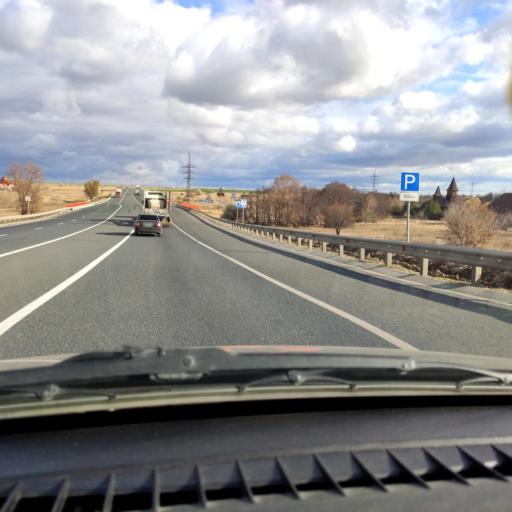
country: RU
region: Samara
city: Varlamovo
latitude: 53.2023
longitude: 48.3798
